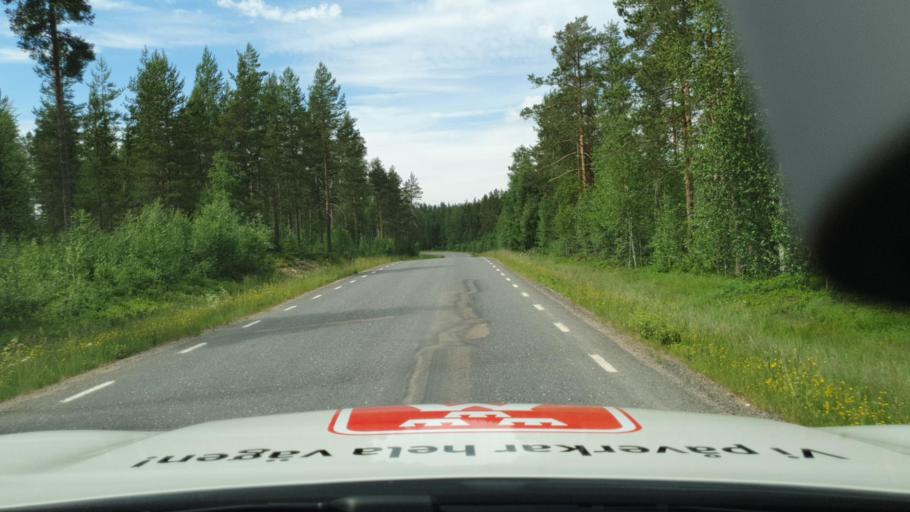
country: SE
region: Vaermland
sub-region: Torsby Kommun
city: Torsby
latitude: 60.6784
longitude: 12.6691
